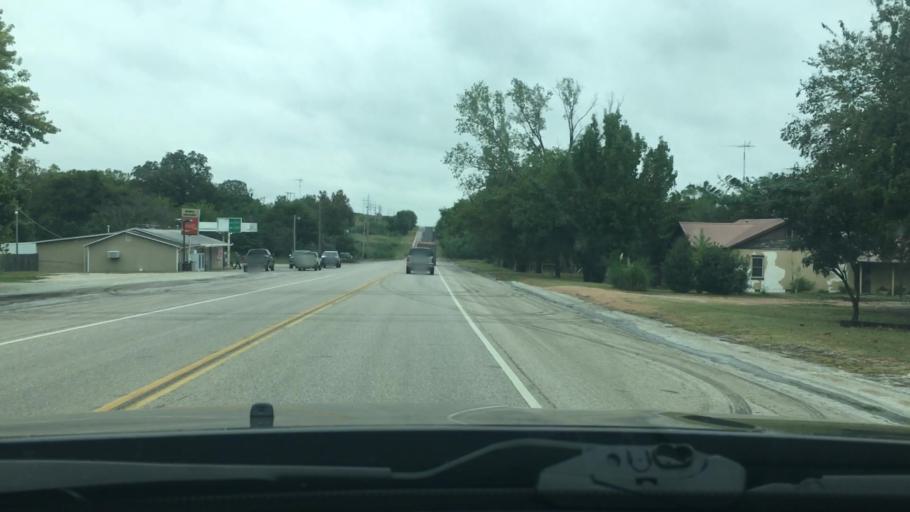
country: US
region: Oklahoma
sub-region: Pontotoc County
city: Ada
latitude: 34.6148
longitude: -96.6348
